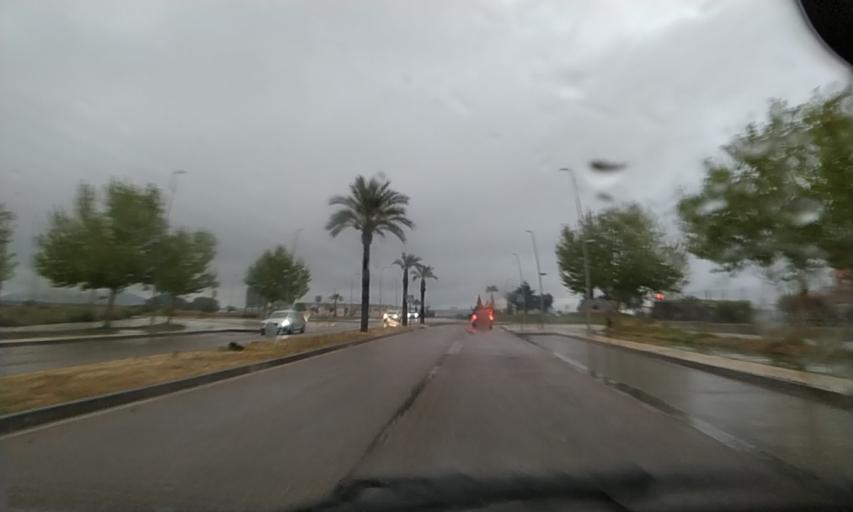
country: ES
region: Extremadura
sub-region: Provincia de Badajoz
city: Merida
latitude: 38.9146
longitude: -6.3636
